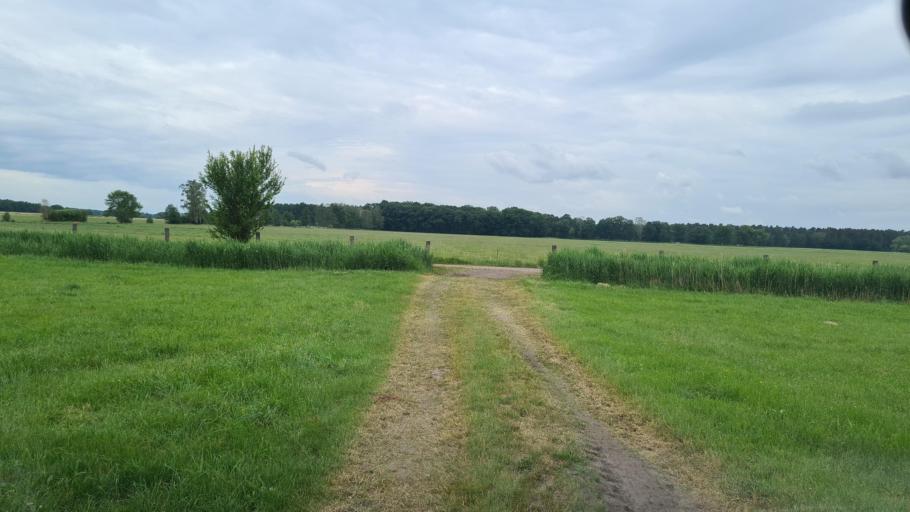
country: DE
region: Brandenburg
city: Bronkow
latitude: 51.6212
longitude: 13.9367
